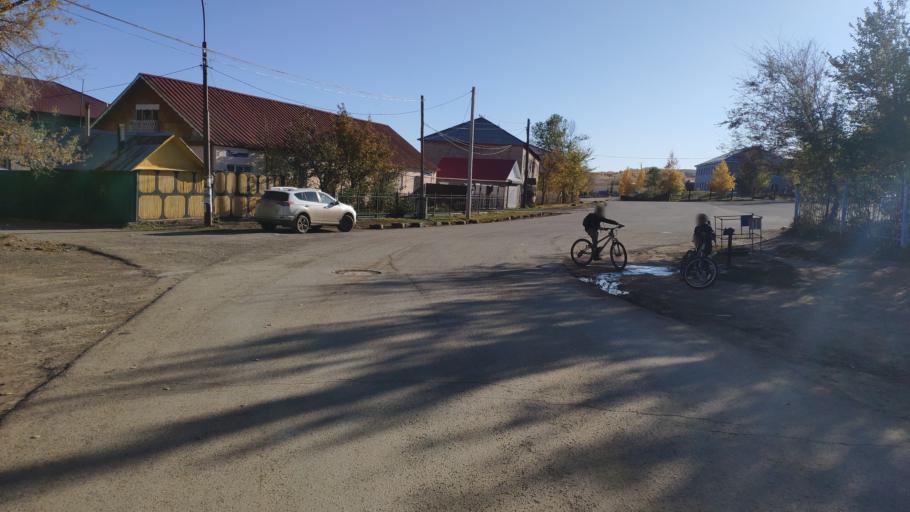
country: RU
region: Bashkortostan
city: Abzakovo
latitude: 53.3406
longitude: 58.5043
